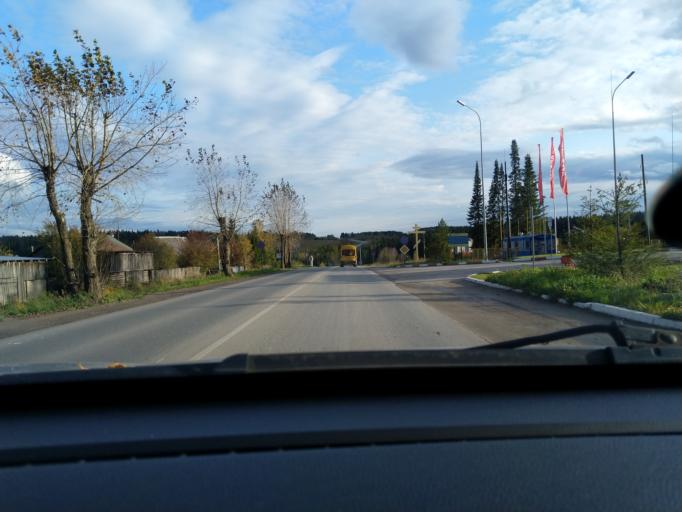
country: RU
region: Perm
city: Polazna
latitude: 58.2832
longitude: 56.4113
